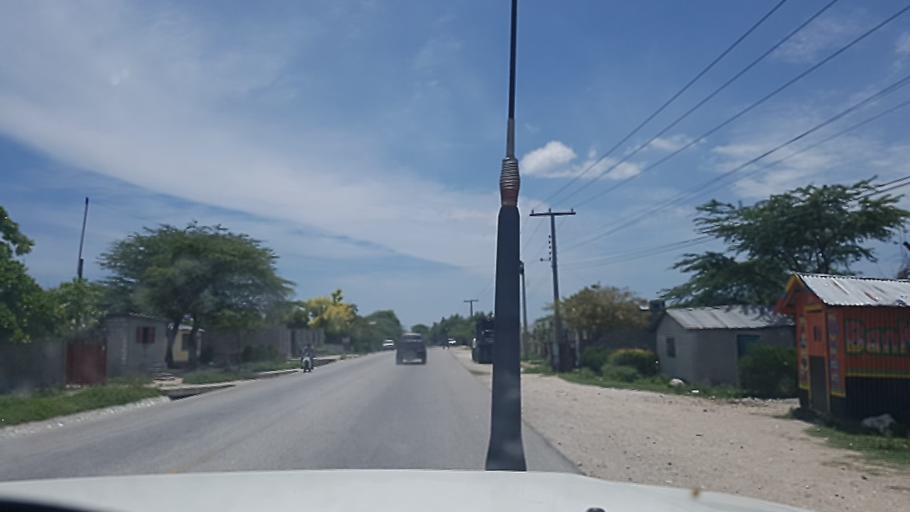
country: HT
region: Artibonite
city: Saint-Marc
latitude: 19.1512
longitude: -72.6236
